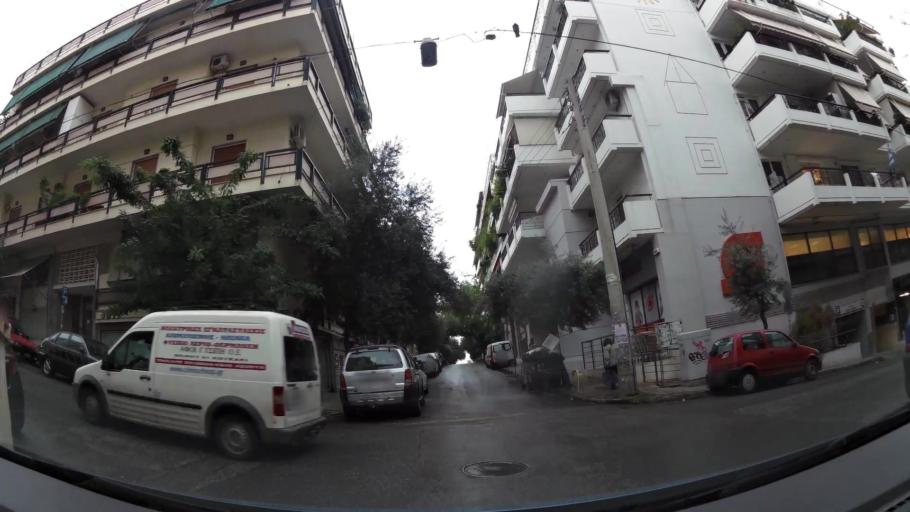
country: GR
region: Attica
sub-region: Nomarchia Athinas
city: Vyronas
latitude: 37.9610
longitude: 23.7446
